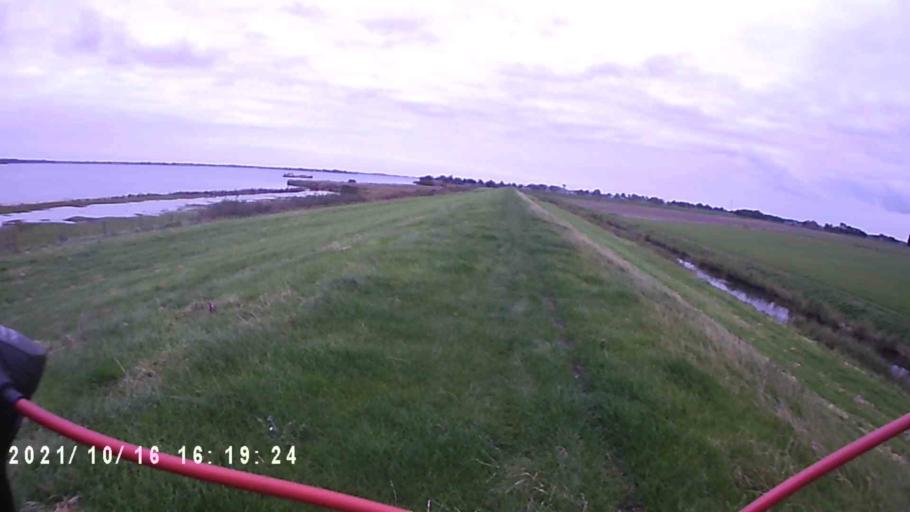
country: NL
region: Friesland
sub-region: Gemeente Dongeradeel
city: Anjum
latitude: 53.3904
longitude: 6.1537
